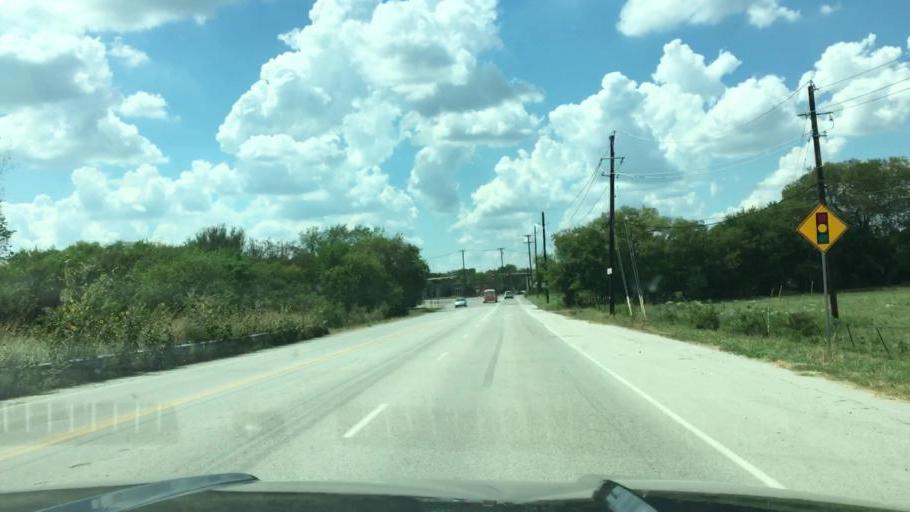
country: US
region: Texas
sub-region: Tarrant County
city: Haslet
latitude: 32.9742
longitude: -97.3451
